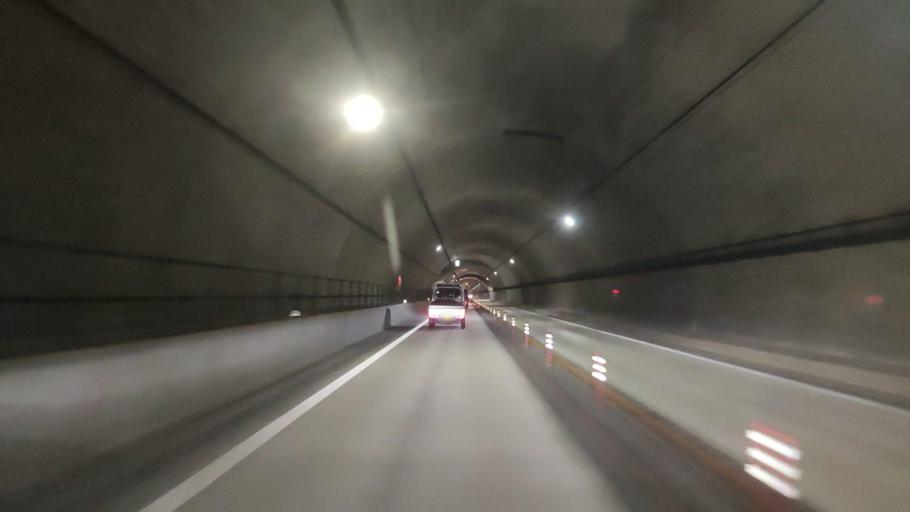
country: JP
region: Wakayama
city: Tanabe
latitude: 33.6151
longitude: 135.4234
